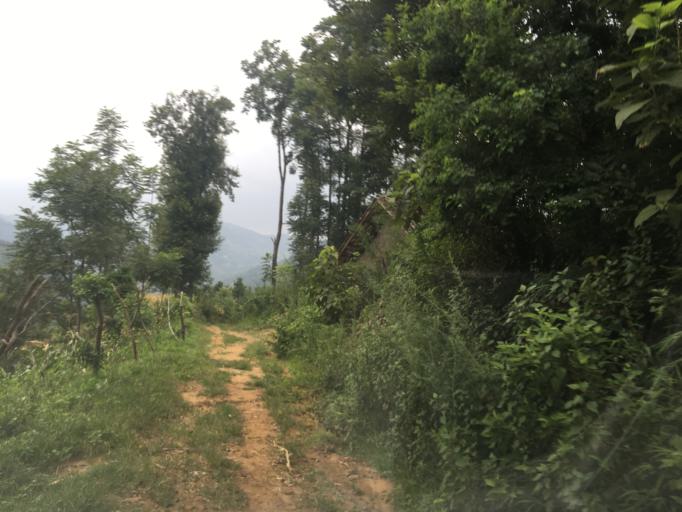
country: CN
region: Guangxi Zhuangzu Zizhiqu
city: Xinzhou
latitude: 25.1656
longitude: 105.6976
